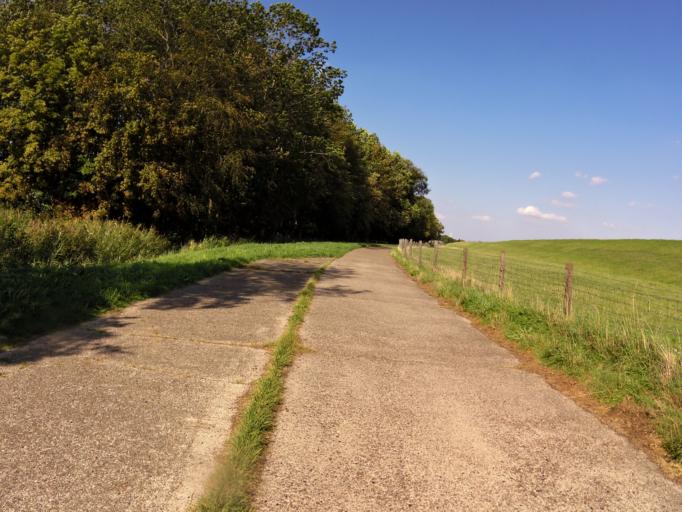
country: DE
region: Lower Saxony
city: Brake (Unterweser)
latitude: 53.4018
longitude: 8.4633
